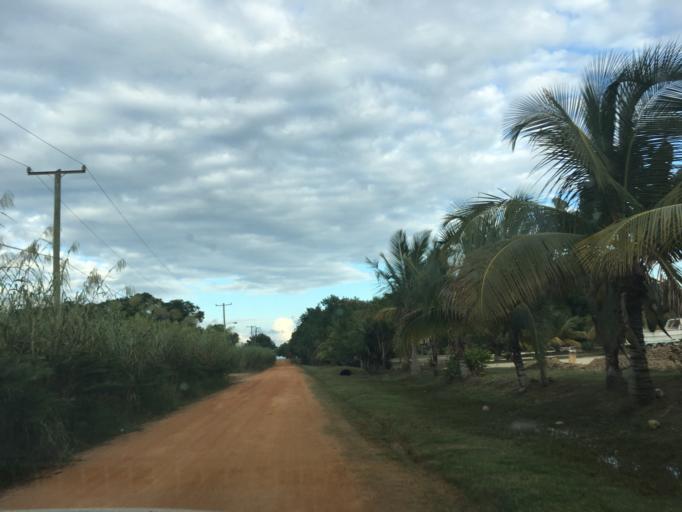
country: BZ
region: Stann Creek
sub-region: Dangriga
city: Dangriga
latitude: 16.8223
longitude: -88.2678
